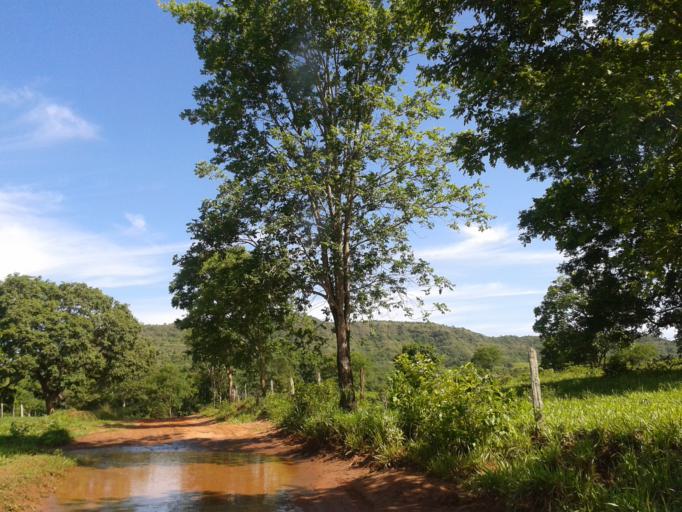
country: BR
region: Minas Gerais
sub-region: Santa Vitoria
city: Santa Vitoria
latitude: -19.0807
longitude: -50.0157
